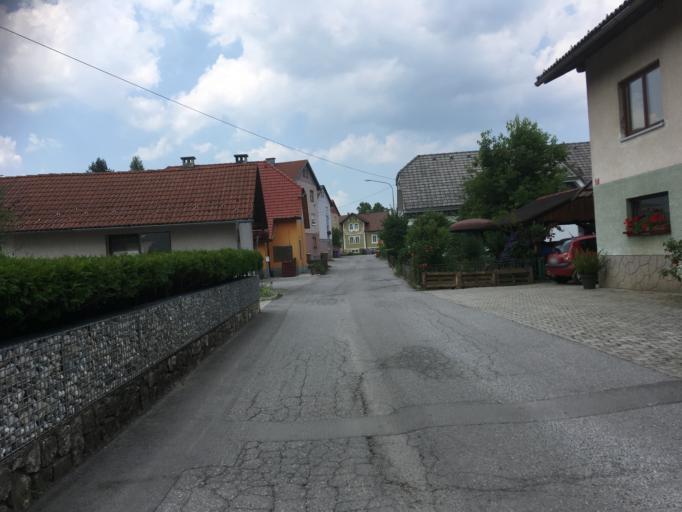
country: SI
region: Kocevje
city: Kocevje
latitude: 45.6403
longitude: 14.8560
